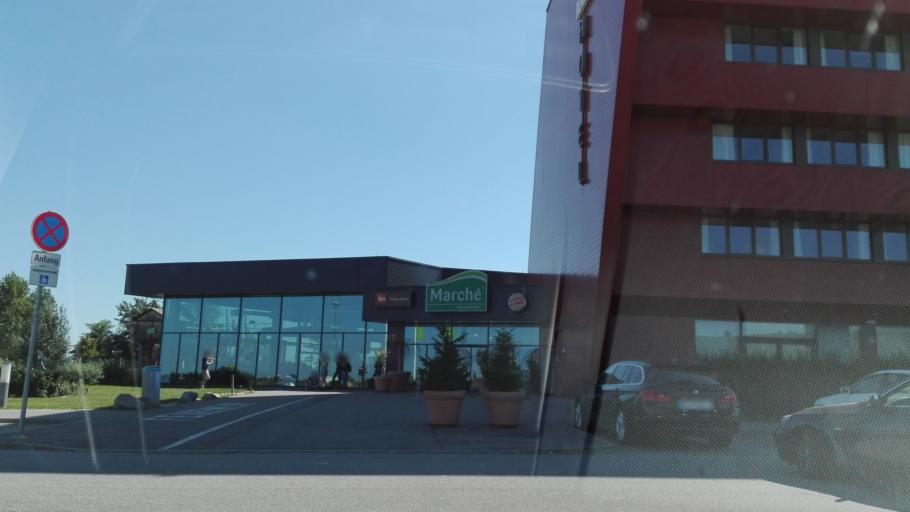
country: AT
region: Lower Austria
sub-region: Politischer Bezirk Wien-Umgebung
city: Lanzendorf
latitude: 48.1231
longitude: 16.4398
